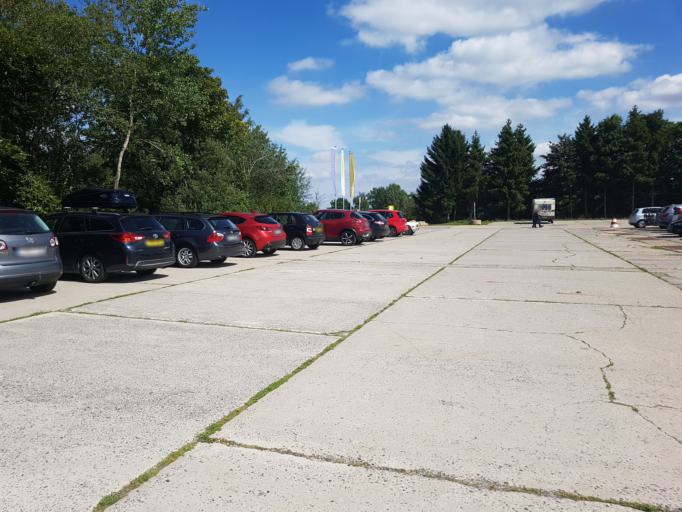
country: DE
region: North Rhine-Westphalia
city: Heimbach
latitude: 50.5827
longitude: 6.4469
